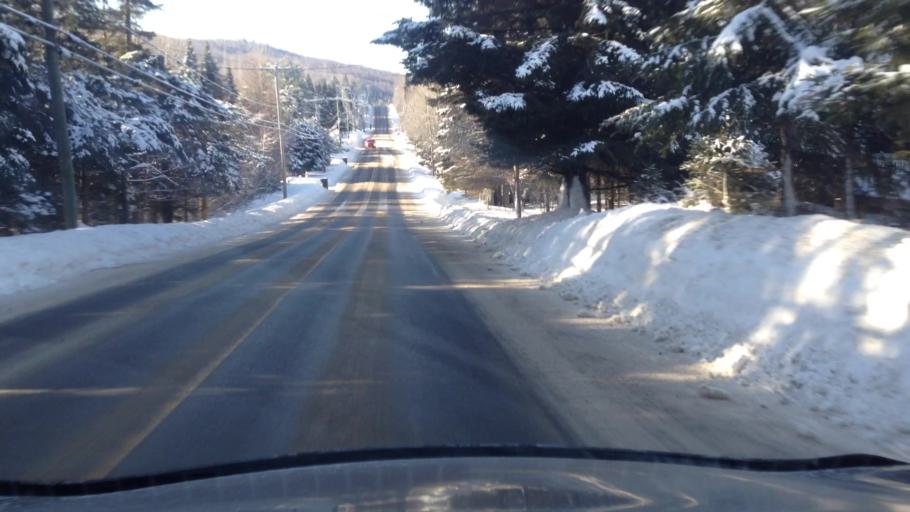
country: CA
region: Quebec
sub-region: Laurentides
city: Sainte-Agathe-des-Monts
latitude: 45.9306
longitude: -74.4194
